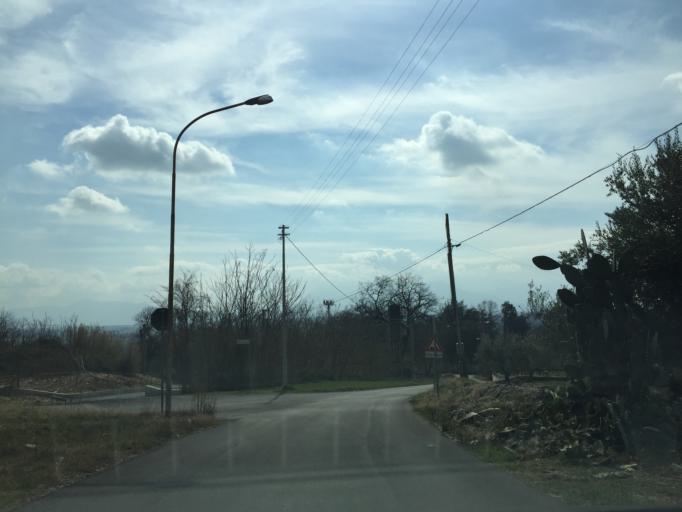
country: IT
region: Latium
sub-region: Provincia di Frosinone
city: Castrocielo
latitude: 41.5246
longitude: 13.7033
